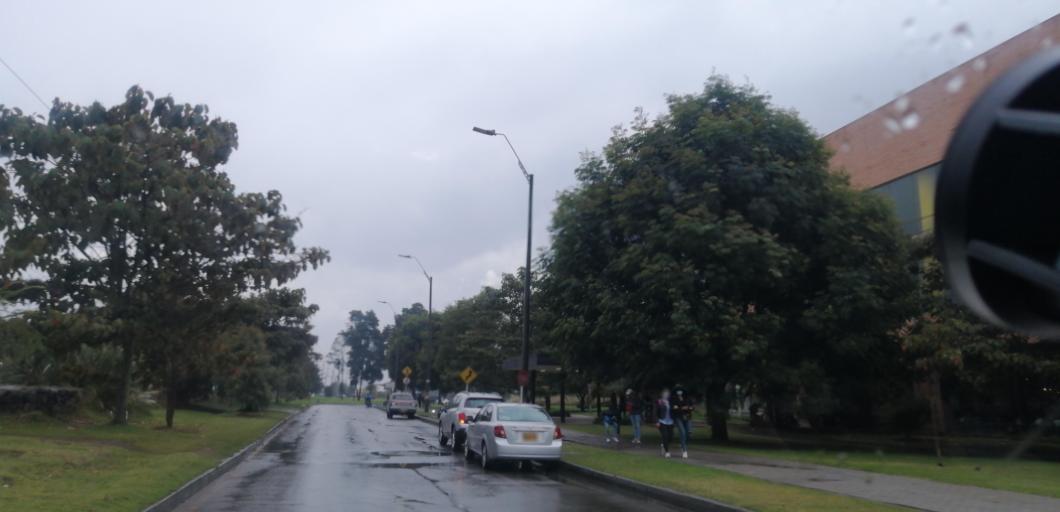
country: CO
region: Cundinamarca
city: Madrid
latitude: 4.7278
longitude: -74.2567
